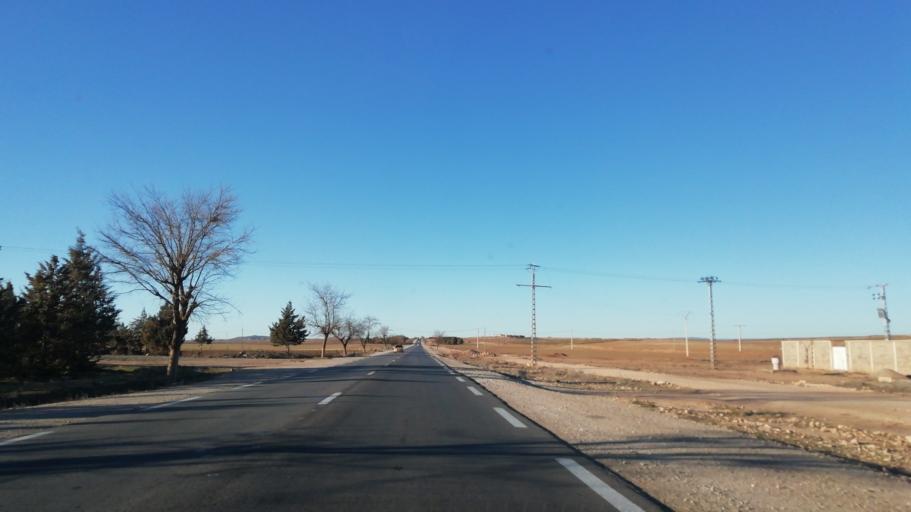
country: DZ
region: Tlemcen
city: Sebdou
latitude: 34.5190
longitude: -1.2880
